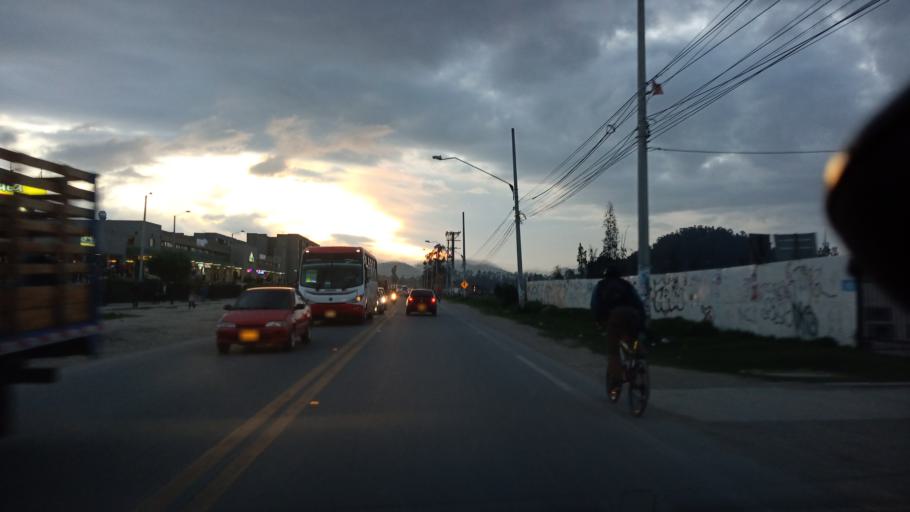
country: CO
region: Cundinamarca
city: Soacha
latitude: 4.5823
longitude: -74.2293
